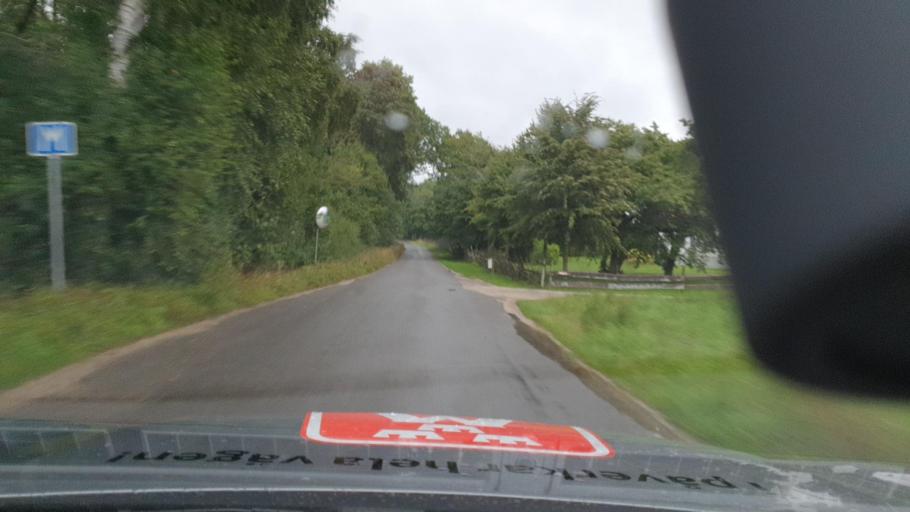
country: SE
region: Gotland
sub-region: Gotland
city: Slite
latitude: 57.7949
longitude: 18.5369
